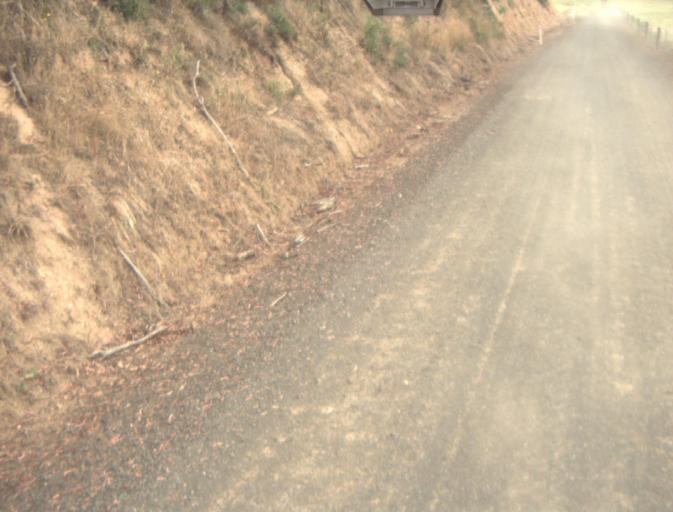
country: AU
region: Tasmania
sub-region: Northern Midlands
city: Evandale
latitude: -41.4684
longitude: 147.5355
